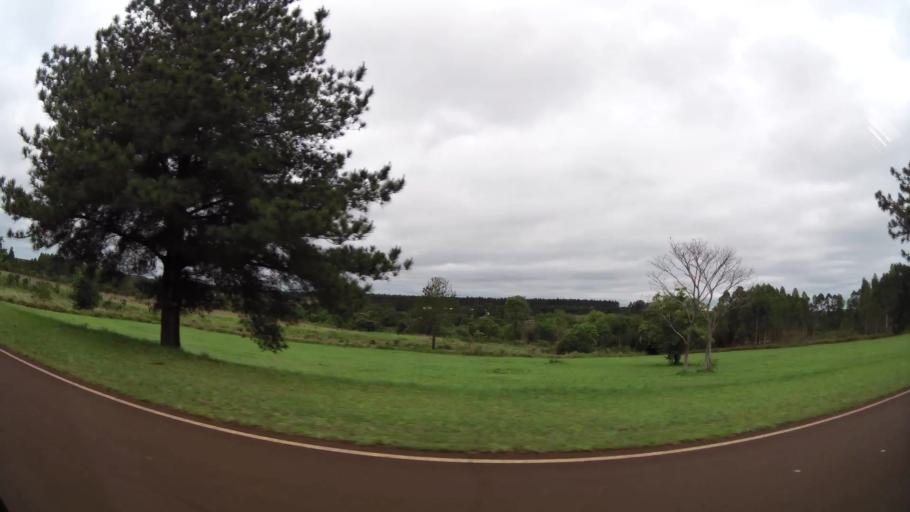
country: PY
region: Alto Parana
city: Colonia Yguazu
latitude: -25.4630
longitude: -54.8433
